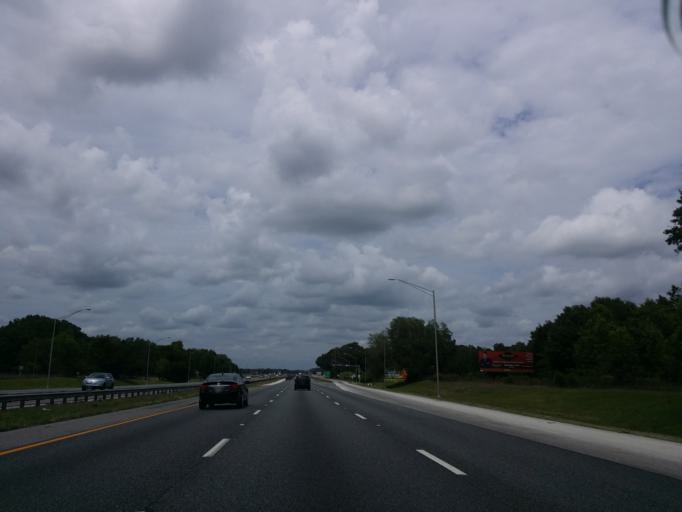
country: US
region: Florida
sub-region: Marion County
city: Belleview
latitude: 28.9842
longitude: -82.1376
